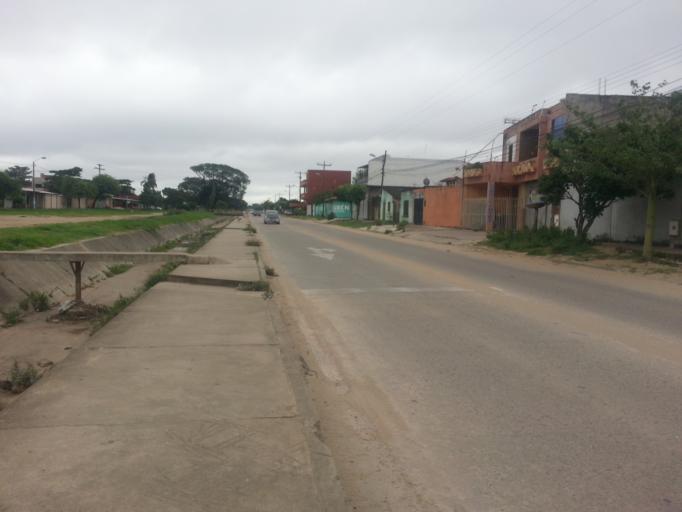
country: BO
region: Santa Cruz
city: Santa Cruz de la Sierra
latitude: -17.8213
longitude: -63.2090
